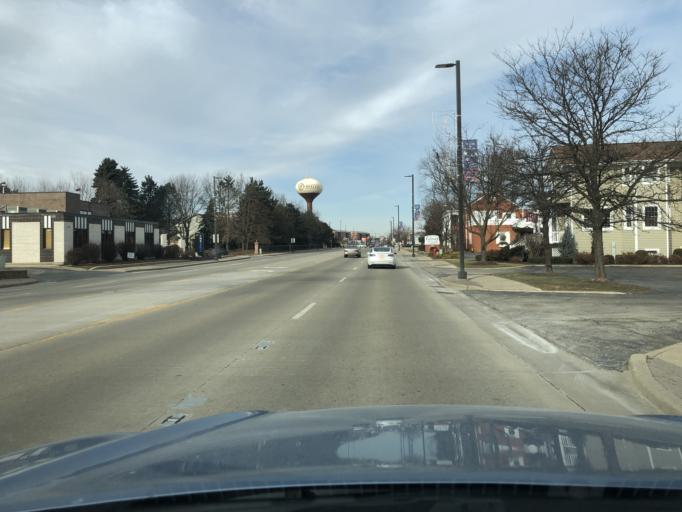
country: US
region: Illinois
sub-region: Cook County
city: Wheeling
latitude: 42.1367
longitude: -87.9045
